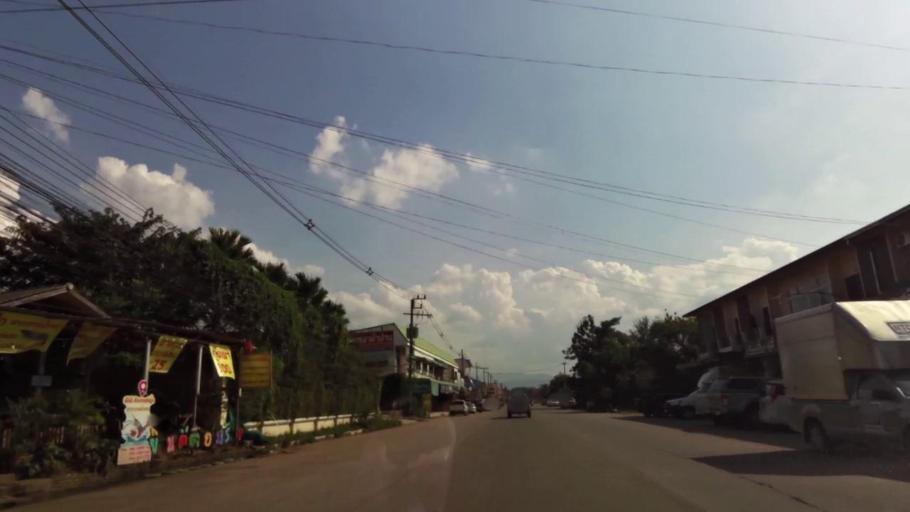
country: TH
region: Phrae
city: Phrae
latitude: 18.1229
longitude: 100.1531
